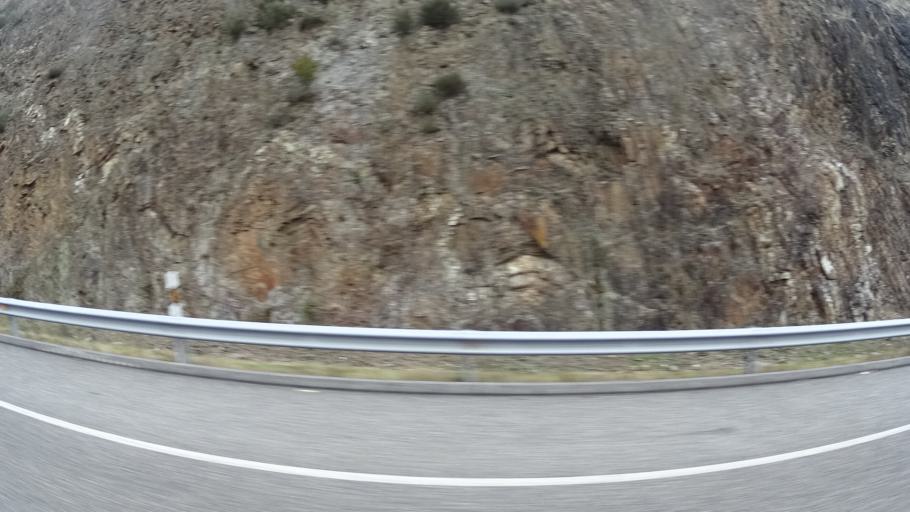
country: ES
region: Galicia
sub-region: Provincia de Lugo
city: Baralla
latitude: 42.9190
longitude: -7.2175
